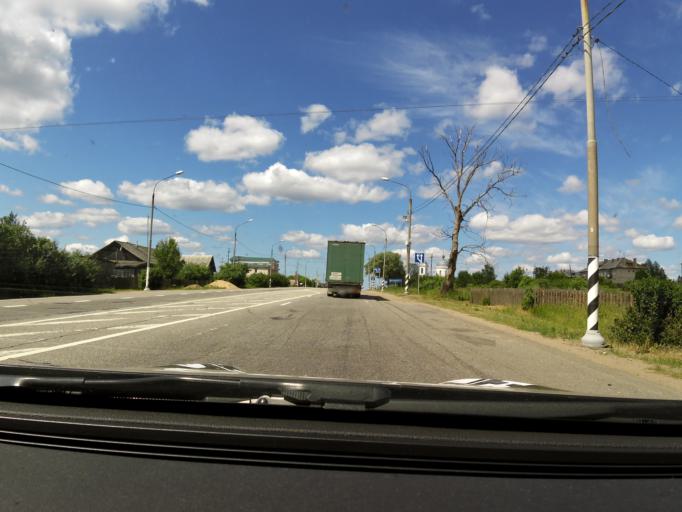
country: RU
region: Tverskaya
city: Kuzhenkino
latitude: 57.7598
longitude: 33.9569
